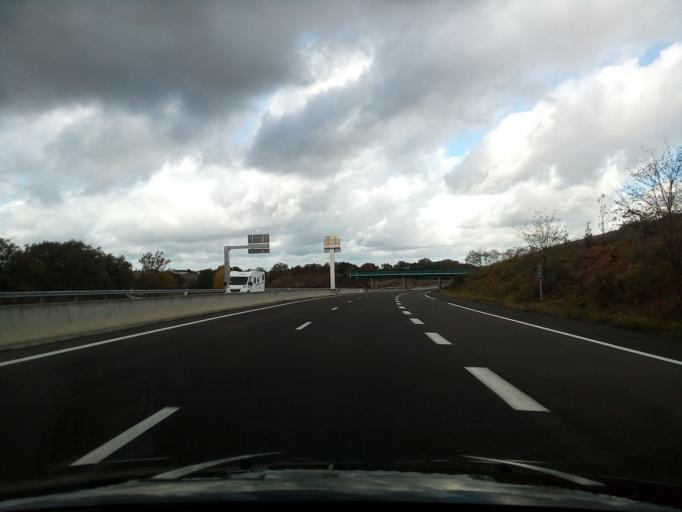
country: FR
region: Auvergne
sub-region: Departement de l'Allier
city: Premilhat
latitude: 46.3358
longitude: 2.5359
